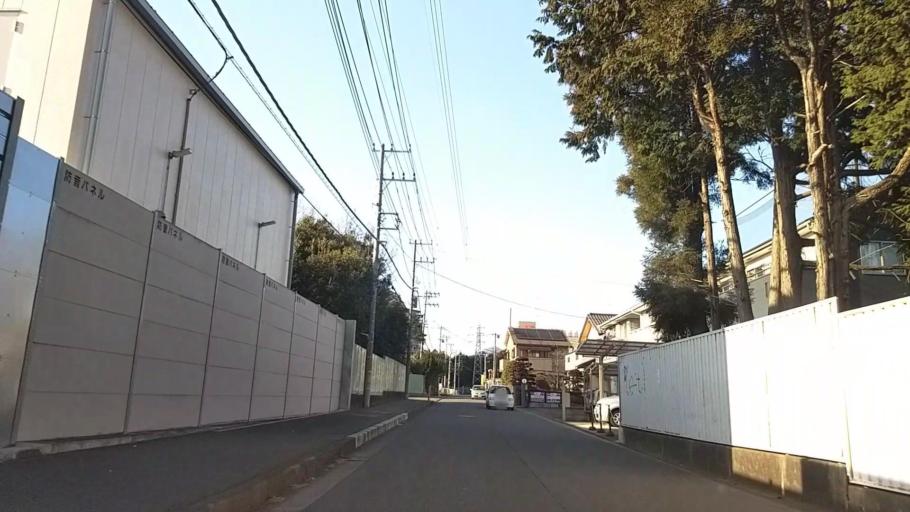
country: JP
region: Kanagawa
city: Atsugi
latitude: 35.4528
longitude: 139.3358
